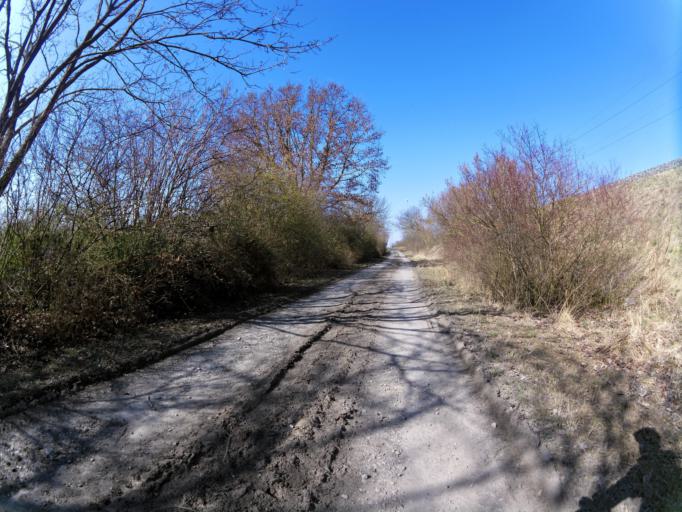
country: DE
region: Bavaria
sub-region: Regierungsbezirk Unterfranken
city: Oberpleichfeld
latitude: 49.8834
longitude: 10.0900
